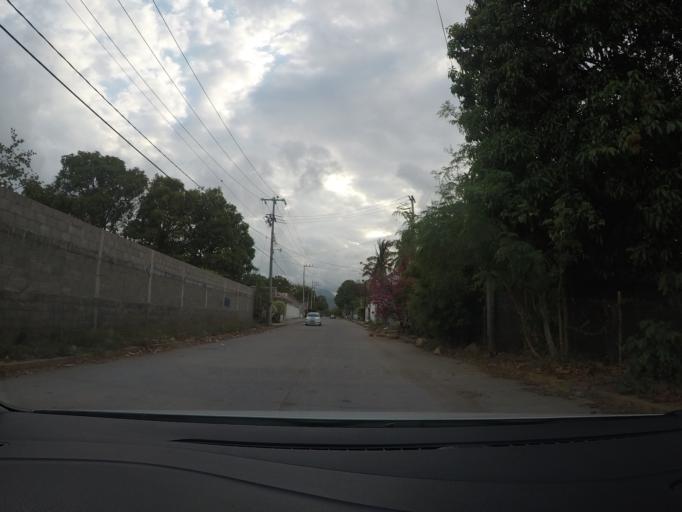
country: MX
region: Oaxaca
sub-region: Salina Cruz
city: Salina Cruz
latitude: 16.2074
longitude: -95.1968
